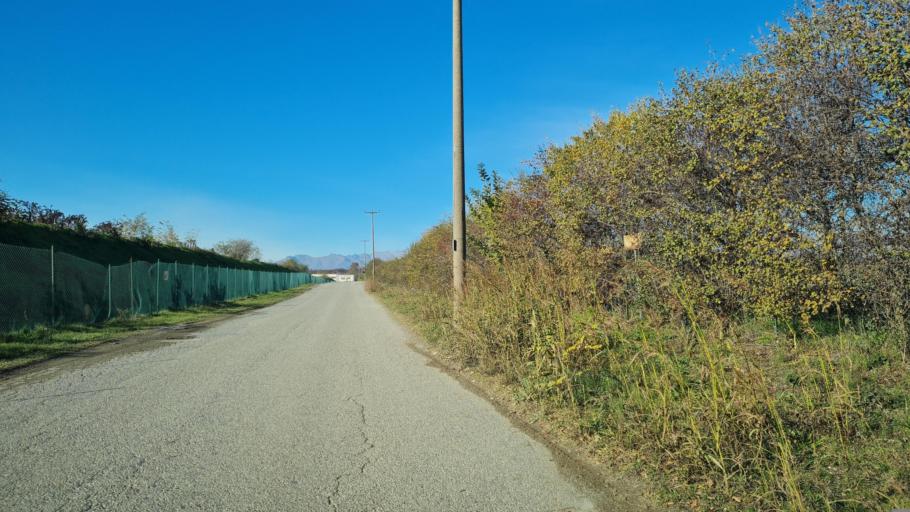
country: IT
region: Piedmont
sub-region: Provincia di Biella
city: Cavaglia
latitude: 45.3851
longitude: 8.0949
